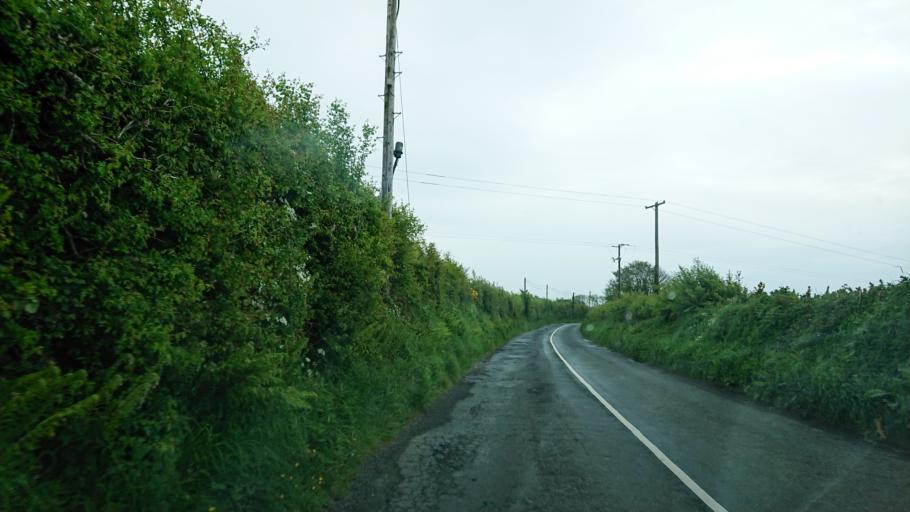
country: IE
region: Munster
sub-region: Waterford
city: Waterford
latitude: 52.2274
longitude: -7.0587
